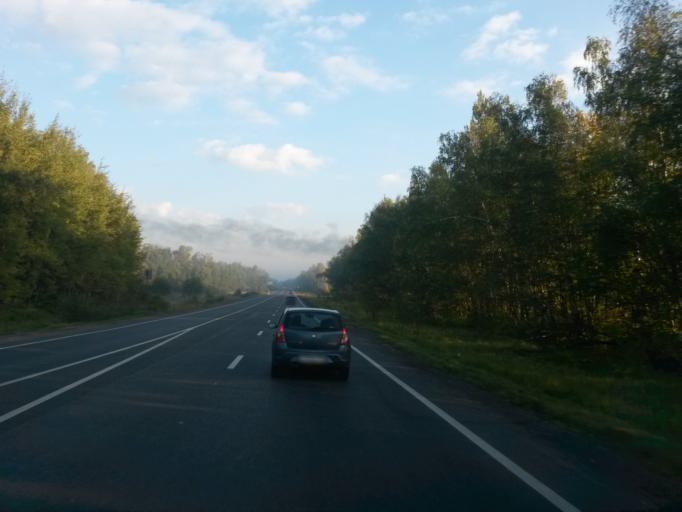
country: RU
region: Moskovskaya
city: Vostryakovo
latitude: 55.3453
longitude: 37.7989
